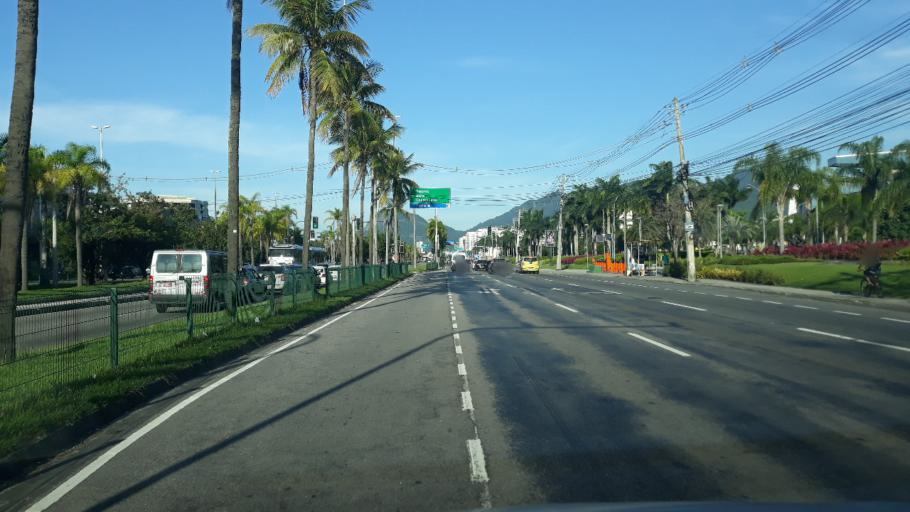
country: BR
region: Rio de Janeiro
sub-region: Sao Joao De Meriti
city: Sao Joao de Meriti
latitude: -22.9732
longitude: -43.3703
